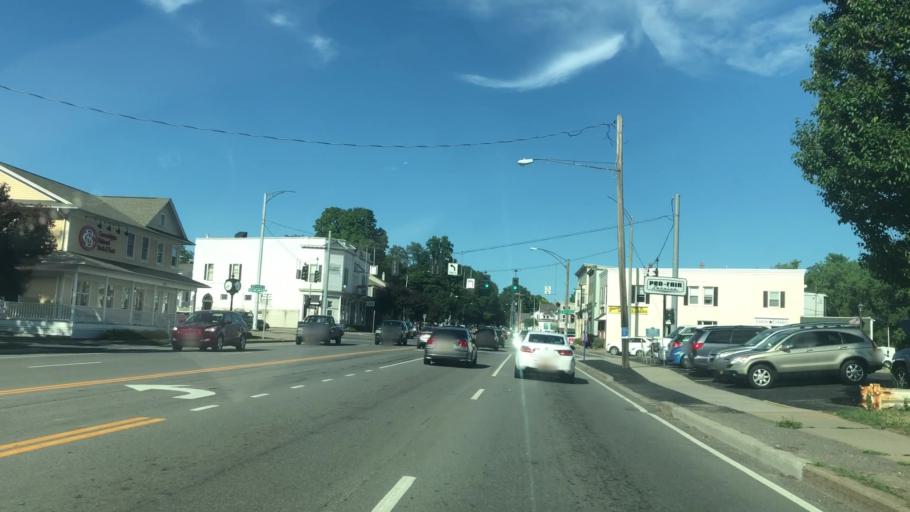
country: US
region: New York
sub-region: Monroe County
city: East Rochester
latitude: 43.1298
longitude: -77.4767
